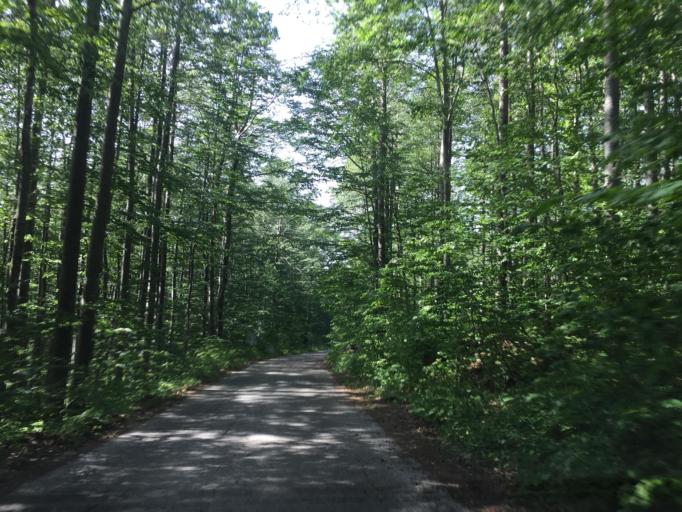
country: HR
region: Primorsko-Goranska
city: Podhum
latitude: 45.4149
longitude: 14.5786
